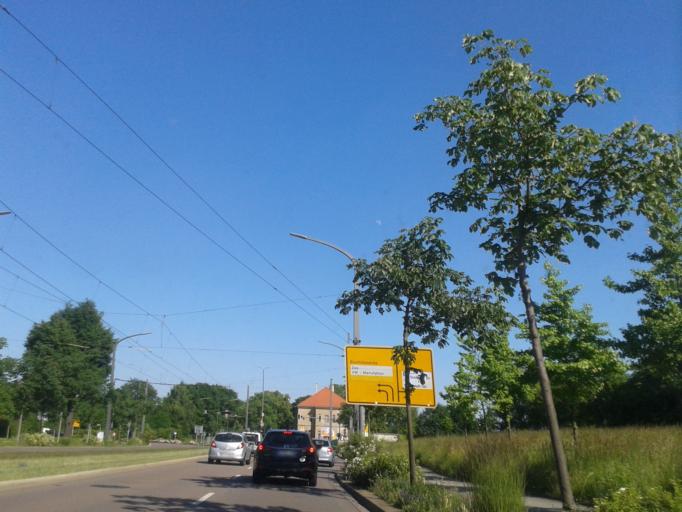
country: DE
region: Saxony
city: Dresden
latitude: 51.0377
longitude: 13.7429
